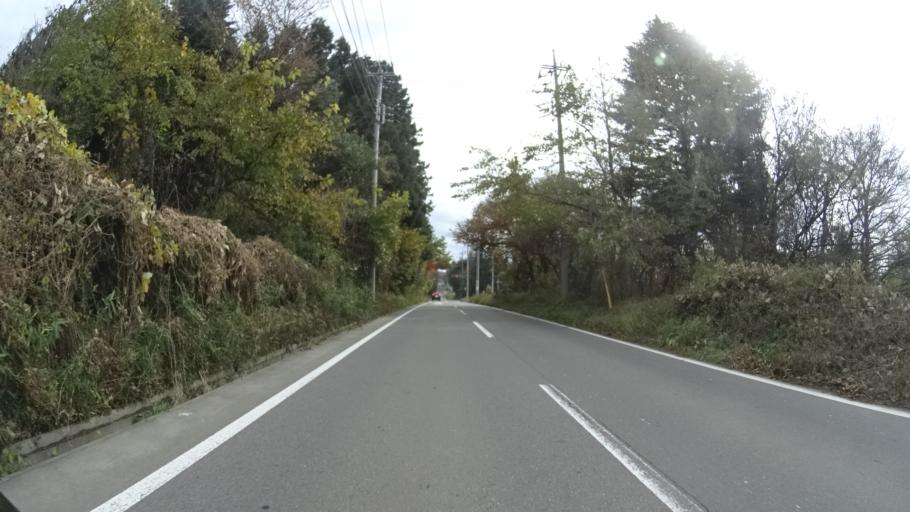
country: JP
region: Gunma
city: Shibukawa
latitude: 36.5228
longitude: 139.0678
